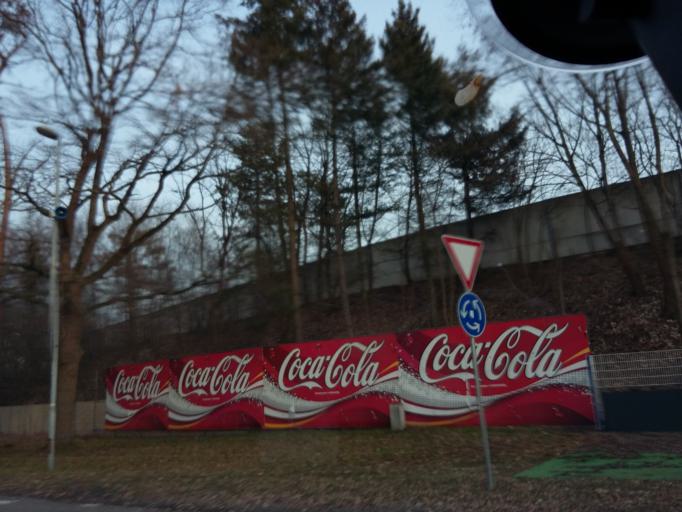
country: DE
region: Baden-Wuerttemberg
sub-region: Karlsruhe Region
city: Hockenheim
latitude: 49.3309
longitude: 8.5631
